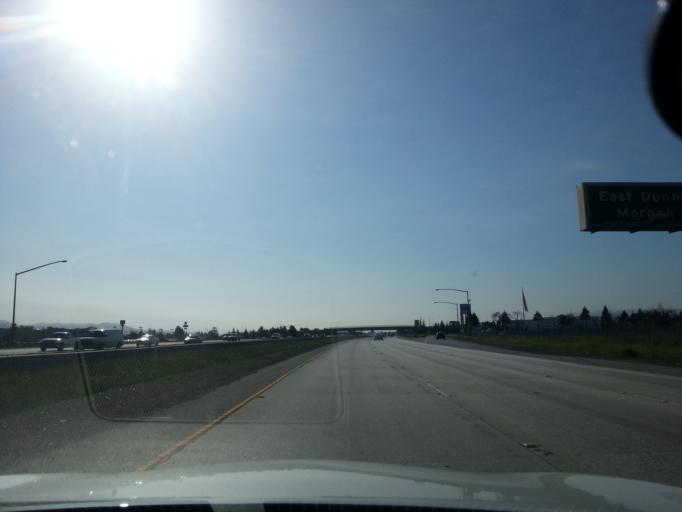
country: US
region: California
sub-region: Santa Clara County
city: Morgan Hill
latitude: 37.1360
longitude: -121.6365
